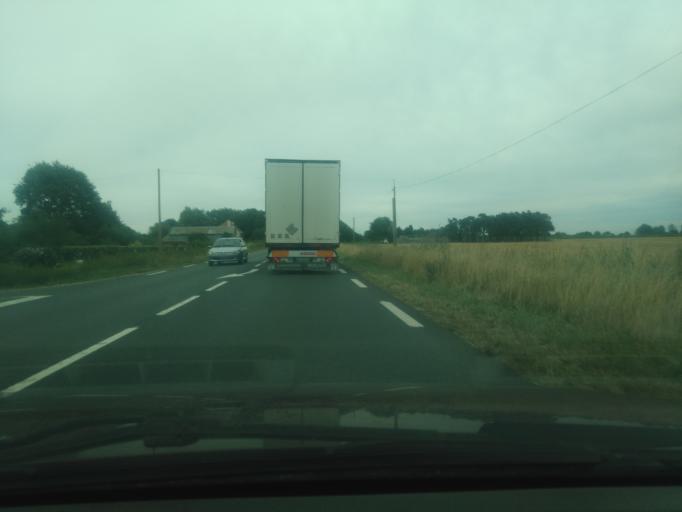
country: FR
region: Poitou-Charentes
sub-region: Departement de la Vienne
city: Lavoux
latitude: 46.5620
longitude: 0.5527
